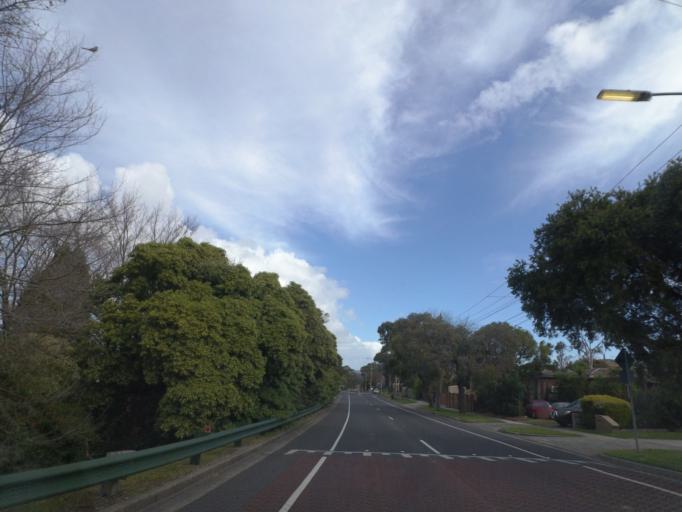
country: AU
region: Victoria
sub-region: Whitehorse
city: Vermont
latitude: -37.8440
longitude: 145.1898
